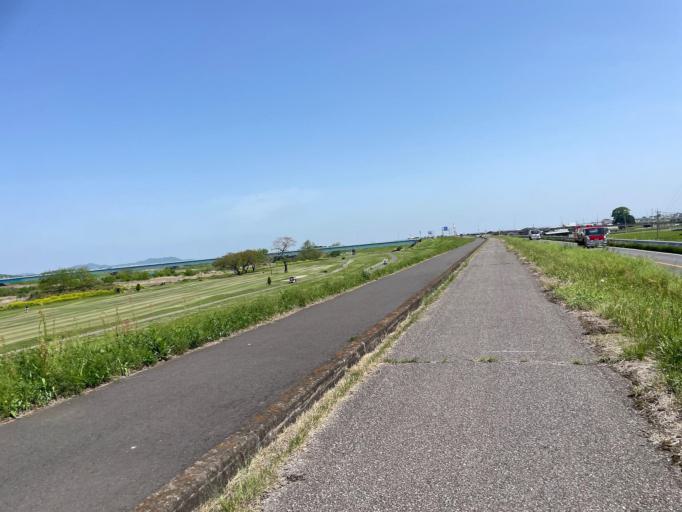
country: JP
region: Tochigi
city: Ashikaga
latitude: 36.3033
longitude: 139.4927
